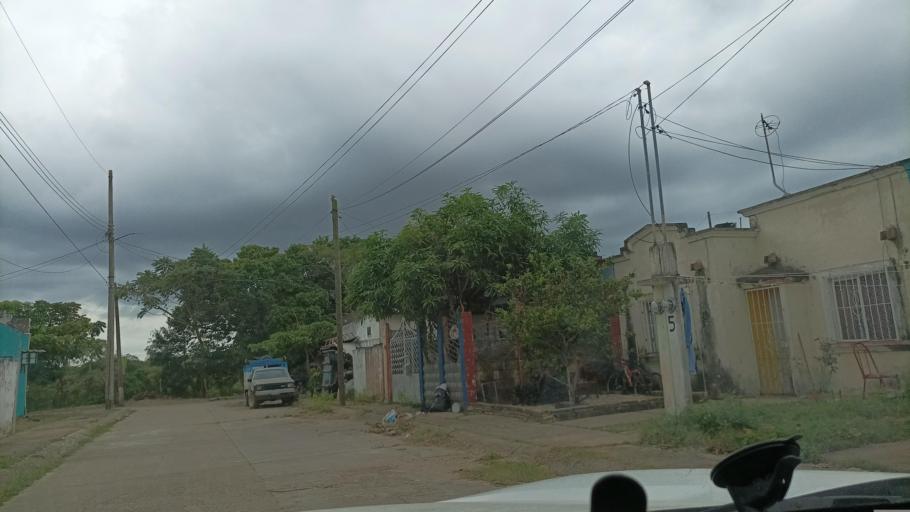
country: MX
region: Veracruz
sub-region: Soconusco
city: Fraccionamiento Santa Cruz
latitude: 17.9706
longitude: -94.8936
